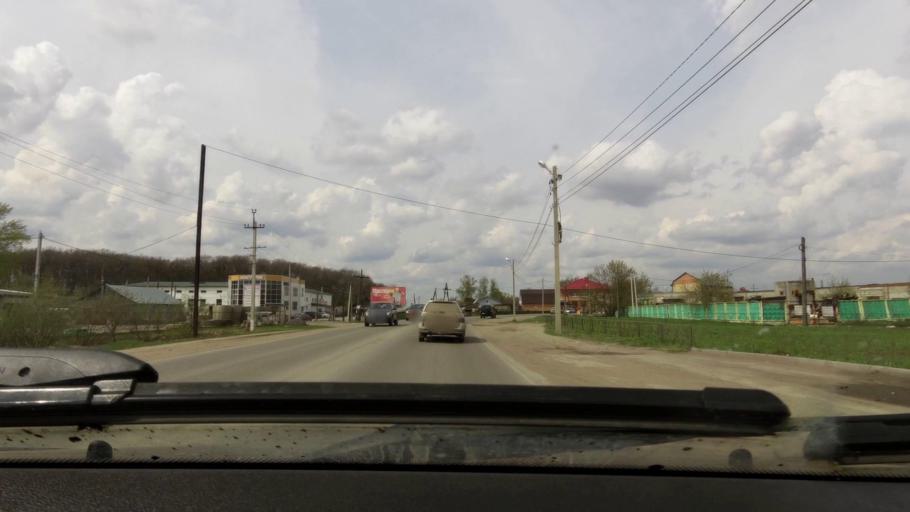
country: RU
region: Rjazan
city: Bagramovo
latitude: 54.7336
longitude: 39.4837
